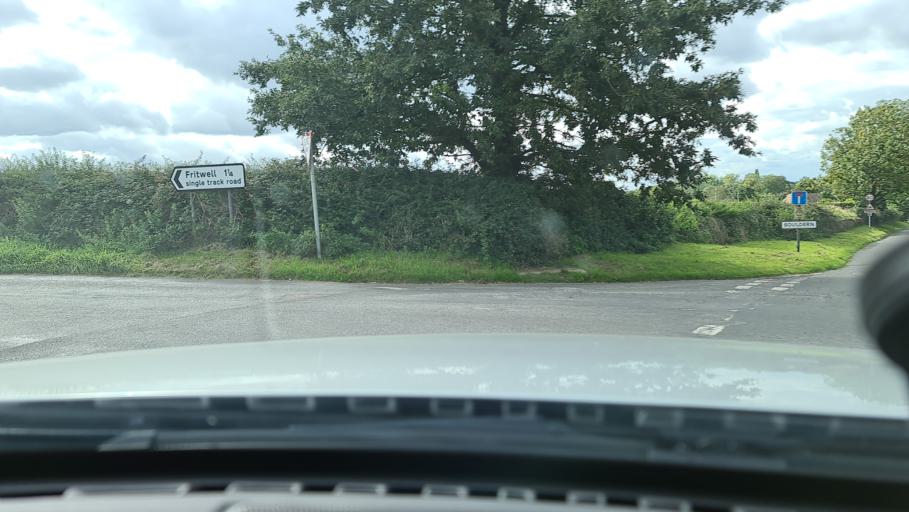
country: GB
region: England
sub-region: Oxfordshire
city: Somerton
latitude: 51.9773
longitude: -1.2352
